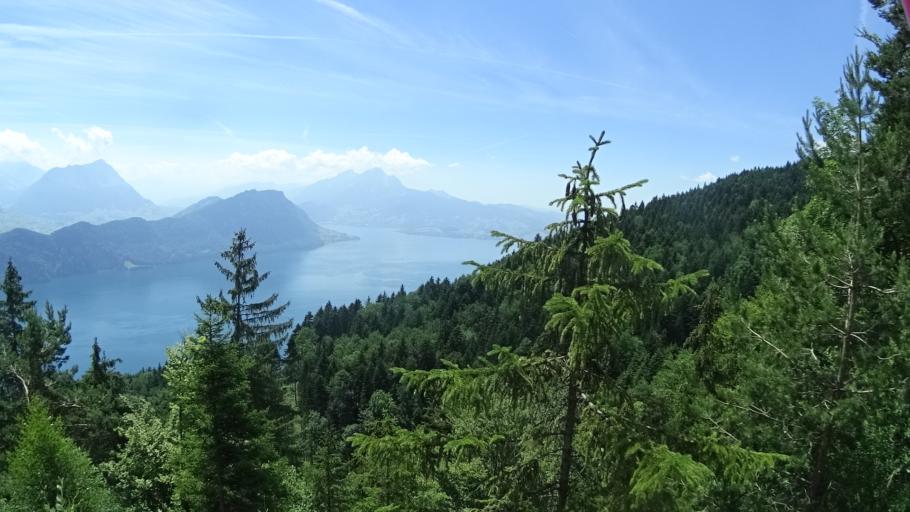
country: CH
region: Lucerne
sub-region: Lucerne-Land District
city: Vitznau
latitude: 47.0311
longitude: 8.4789
